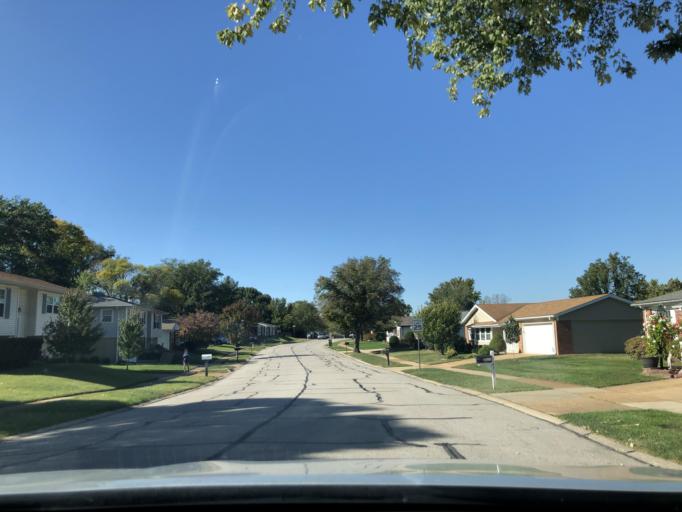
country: US
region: Missouri
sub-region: Saint Louis County
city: Concord
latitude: 38.4958
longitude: -90.3650
